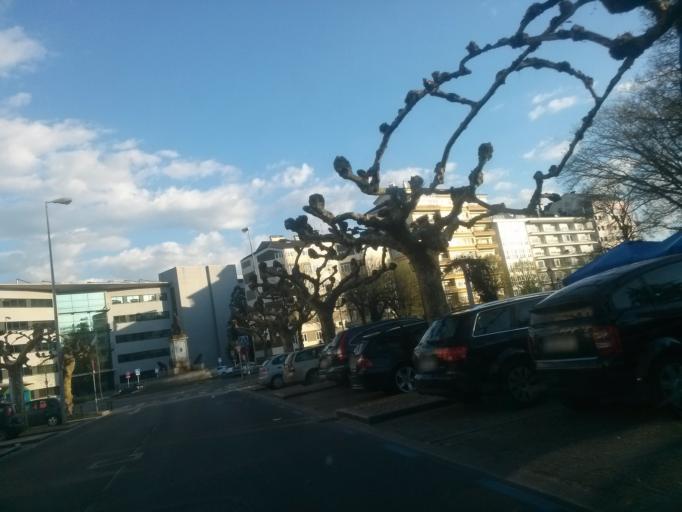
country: ES
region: Galicia
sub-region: Provincia de Lugo
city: Lugo
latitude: 43.0064
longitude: -7.5585
